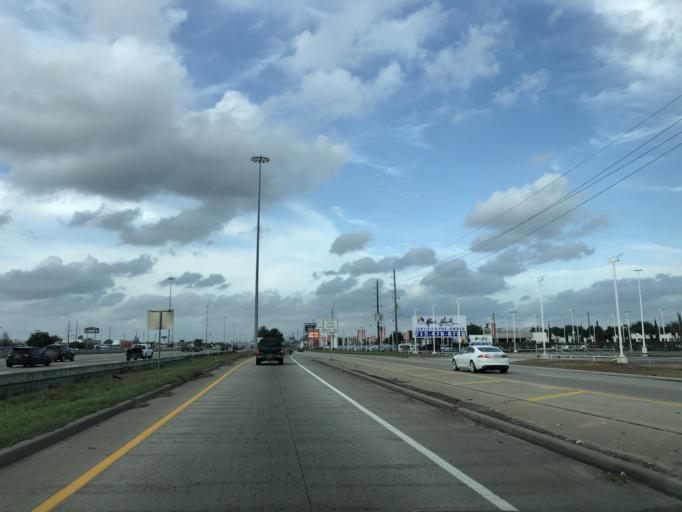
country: US
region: Texas
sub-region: Harris County
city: Spring
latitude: 30.0574
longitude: -95.4324
